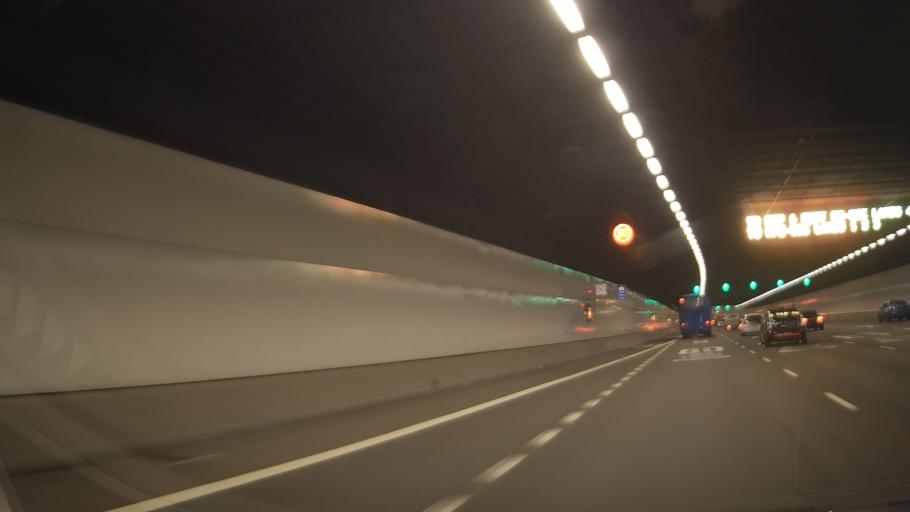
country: SG
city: Singapore
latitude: 1.2753
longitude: 103.8703
